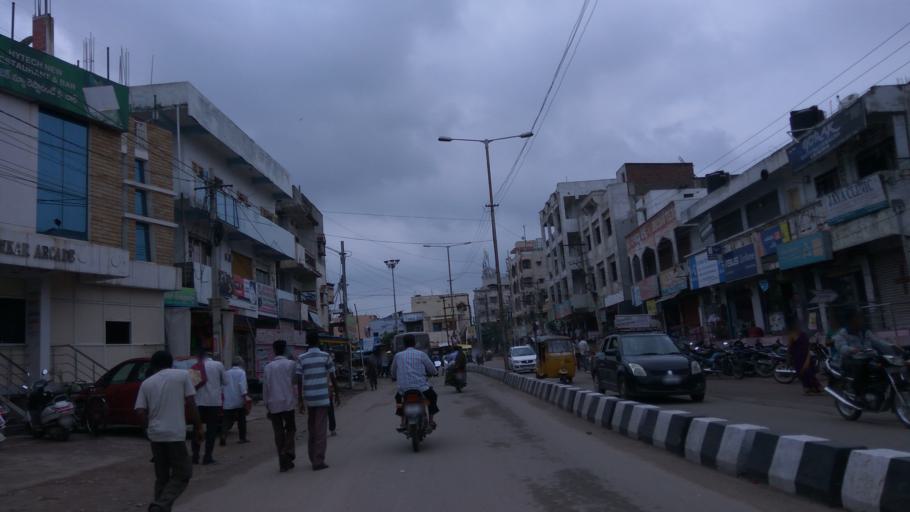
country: IN
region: Telangana
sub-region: Hyderabad
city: Malkajgiri
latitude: 17.4421
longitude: 78.5324
